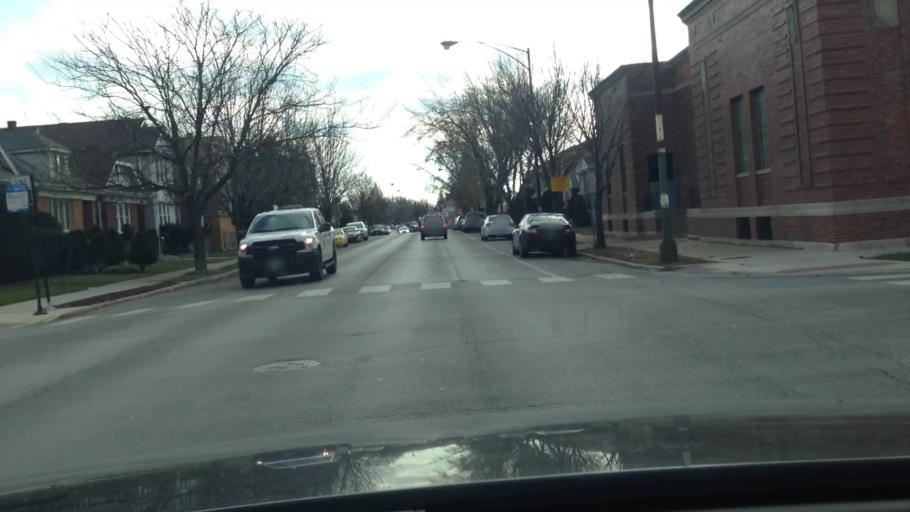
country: US
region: Illinois
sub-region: Cook County
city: Elmwood Park
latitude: 41.9402
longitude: -87.7861
